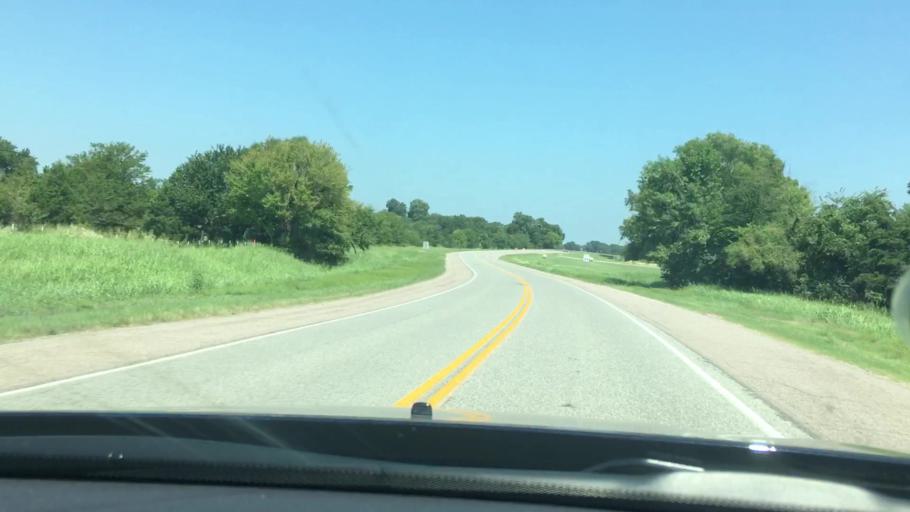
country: US
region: Oklahoma
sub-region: Johnston County
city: Tishomingo
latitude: 34.2458
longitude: -96.5488
